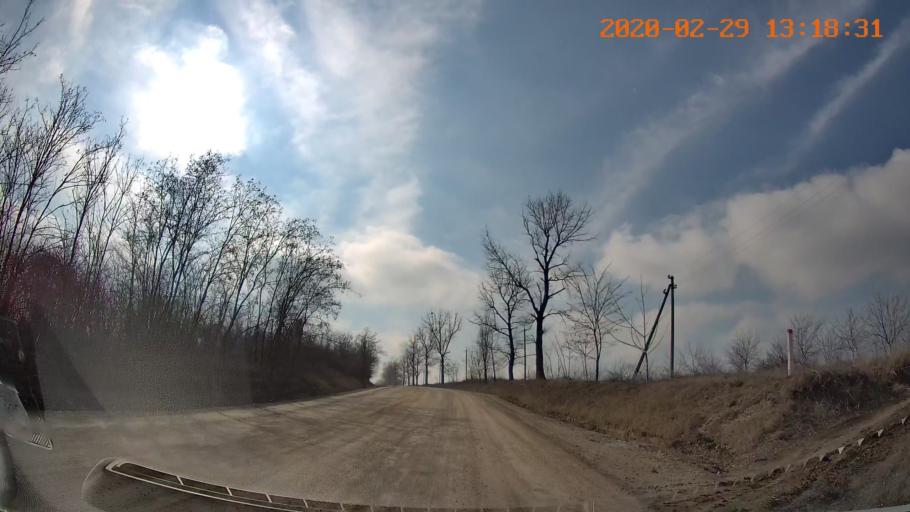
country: MD
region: Telenesti
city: Camenca
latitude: 47.9934
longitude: 28.6569
